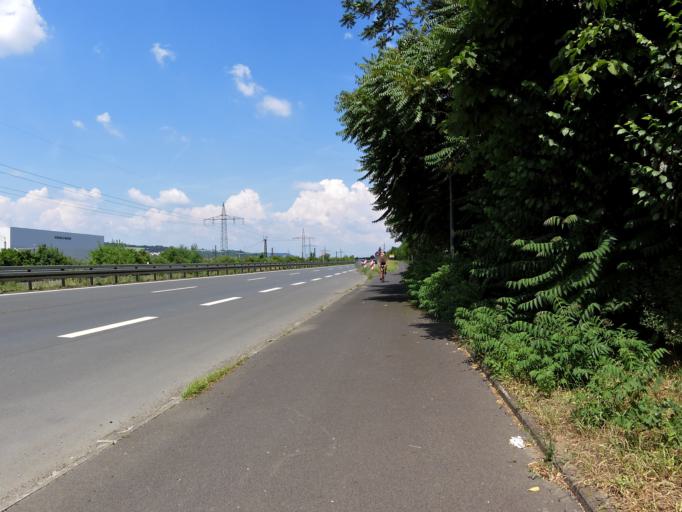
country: DE
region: Bavaria
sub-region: Regierungsbezirk Unterfranken
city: Zell am Main
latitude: 49.8102
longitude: 9.8834
